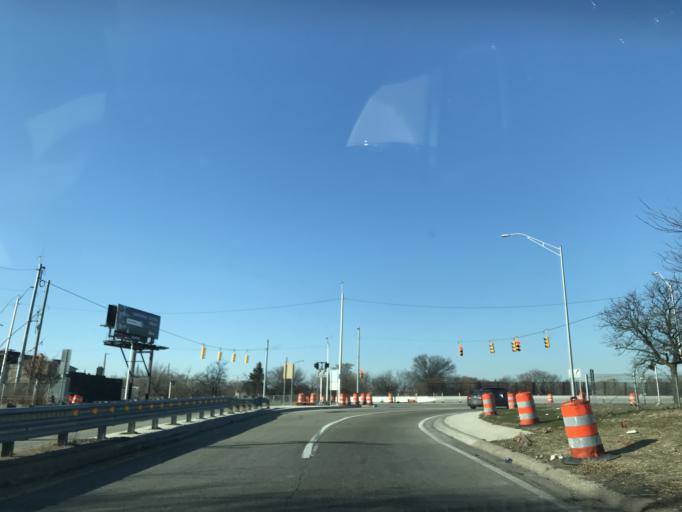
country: US
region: Michigan
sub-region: Wayne County
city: Hamtramck
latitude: 42.3907
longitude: -83.0059
